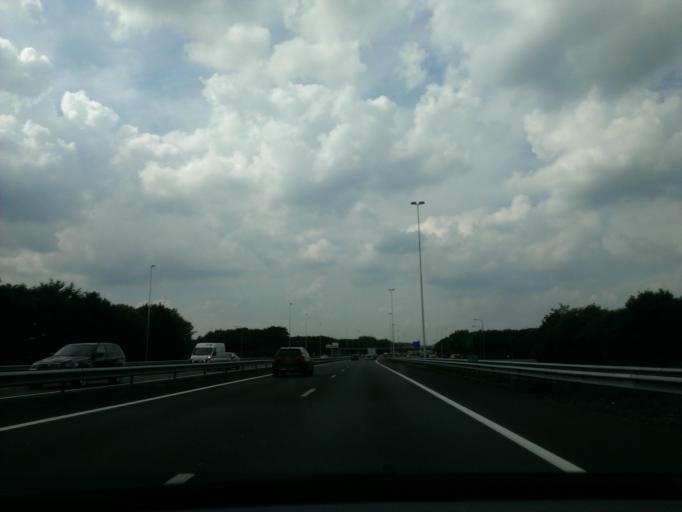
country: NL
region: Utrecht
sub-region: Gemeente Leusden
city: Leusden
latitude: 52.1727
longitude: 5.4342
